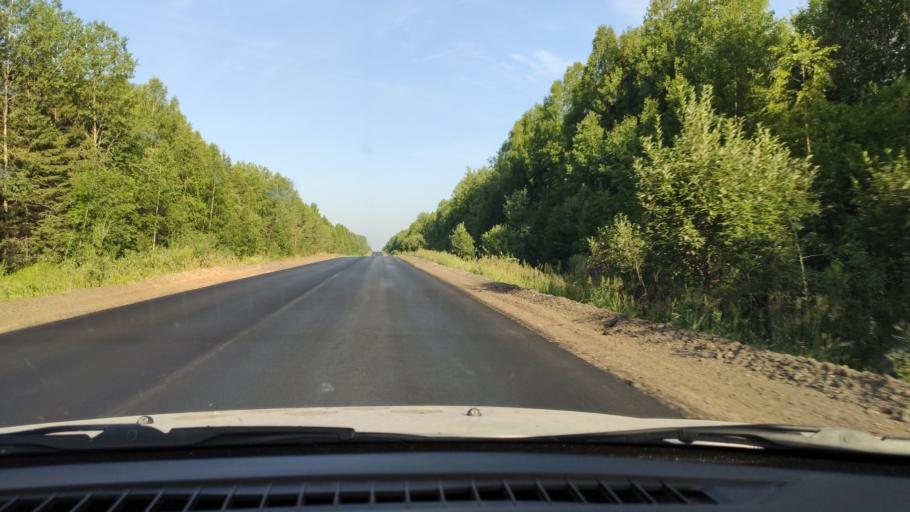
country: RU
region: Kirov
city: Chernaya Kholunitsa
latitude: 58.8795
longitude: 51.4490
